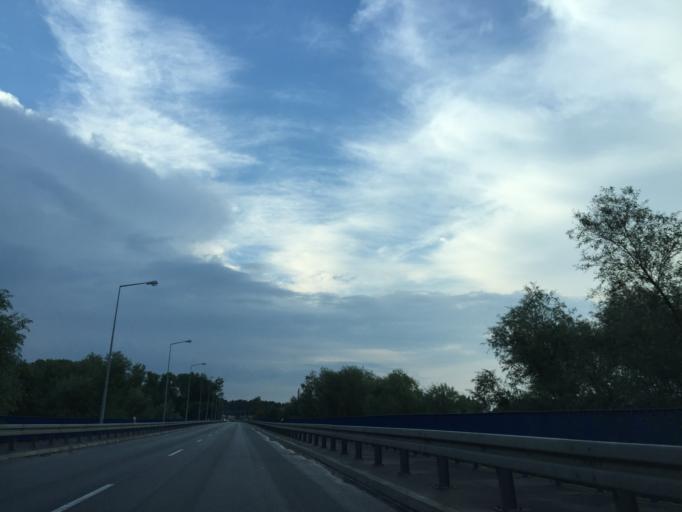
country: PL
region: Masovian Voivodeship
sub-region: Powiat ostrowski
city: Brok
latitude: 52.6935
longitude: 21.8502
